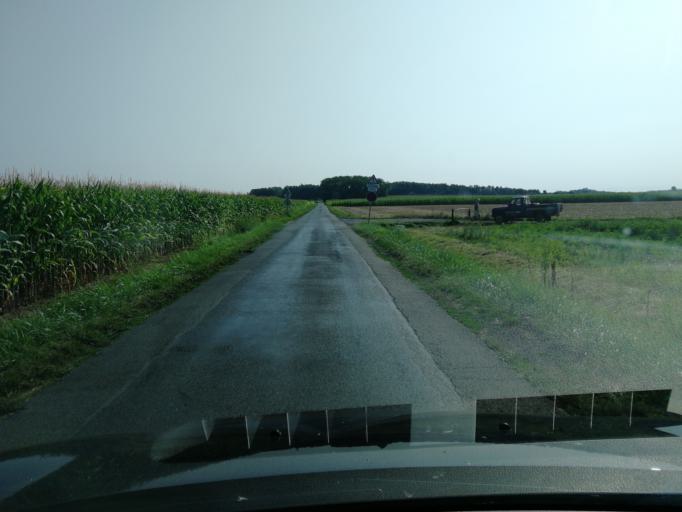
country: FR
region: Rhone-Alpes
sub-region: Departement du Rhone
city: Cailloux-sur-Fontaines
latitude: 45.8499
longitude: 4.9017
